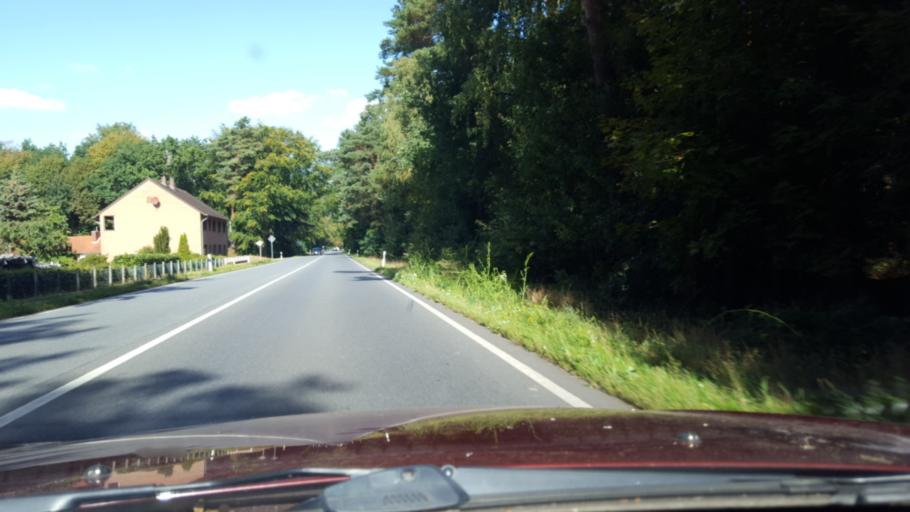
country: DE
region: Lower Saxony
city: Eystrup
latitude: 52.8113
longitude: 9.2016
